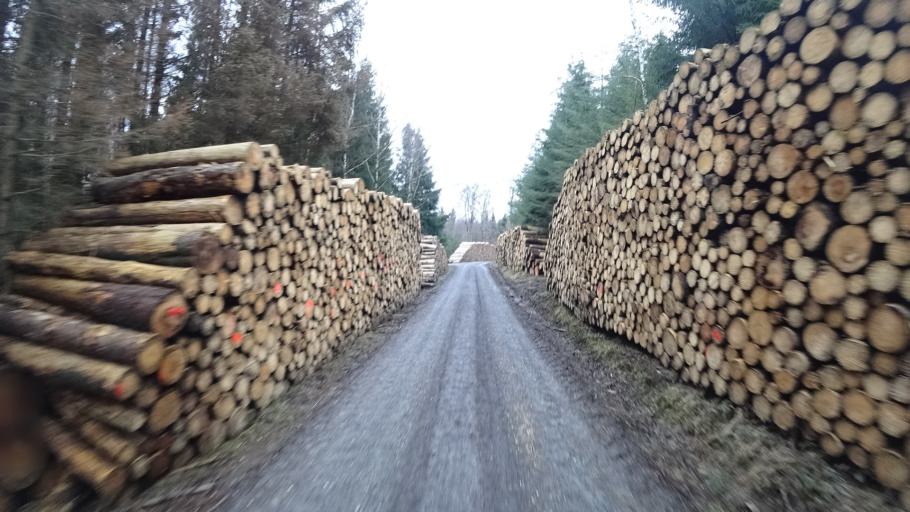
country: DE
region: Rheinland-Pfalz
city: Hillscheid
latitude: 50.4268
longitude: 7.7250
